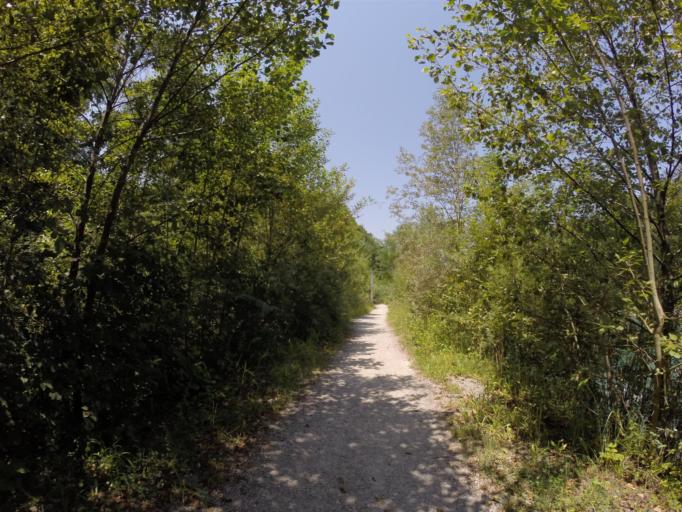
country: CH
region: Bern
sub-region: Bern-Mittelland District
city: Kehrsatz
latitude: 46.9248
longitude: 7.4709
